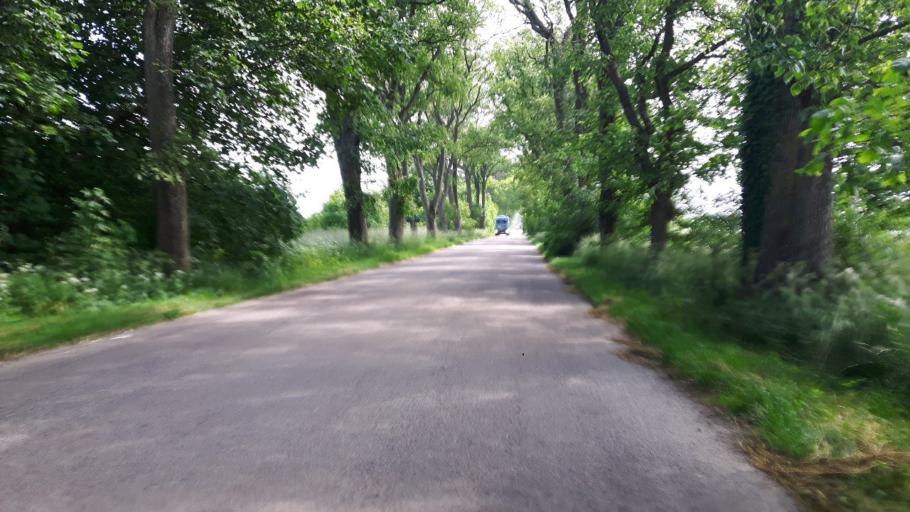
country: PL
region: Pomeranian Voivodeship
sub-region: Powiat wejherowski
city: Choczewo
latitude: 54.7394
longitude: 17.8182
